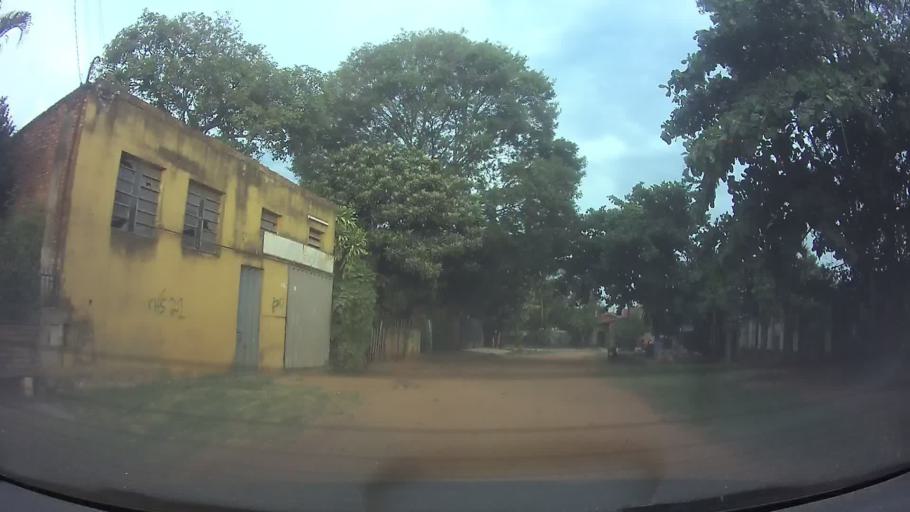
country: PY
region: Central
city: San Lorenzo
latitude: -25.2597
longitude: -57.4634
